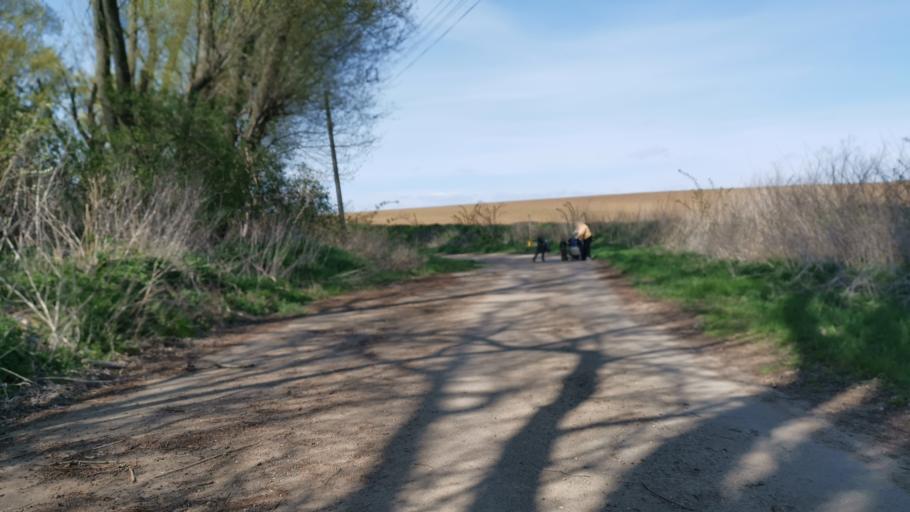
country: SK
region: Trnavsky
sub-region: Okres Skalica
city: Holic
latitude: 48.7728
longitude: 17.1831
